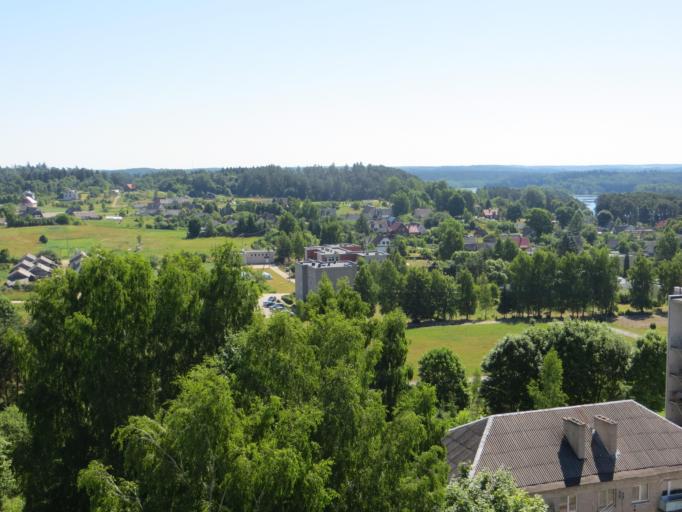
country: LT
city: Aukstadvaris
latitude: 54.5817
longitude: 24.5275
